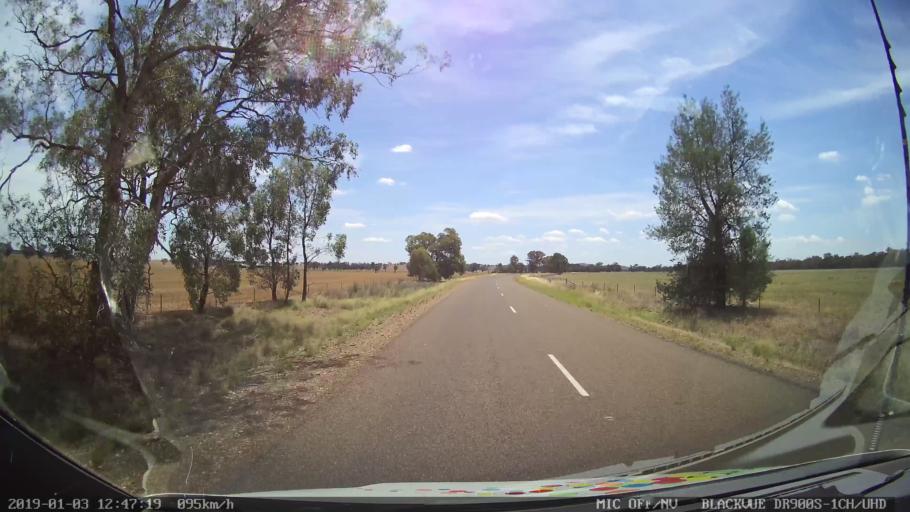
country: AU
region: New South Wales
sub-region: Weddin
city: Grenfell
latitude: -33.7284
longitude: 148.2415
